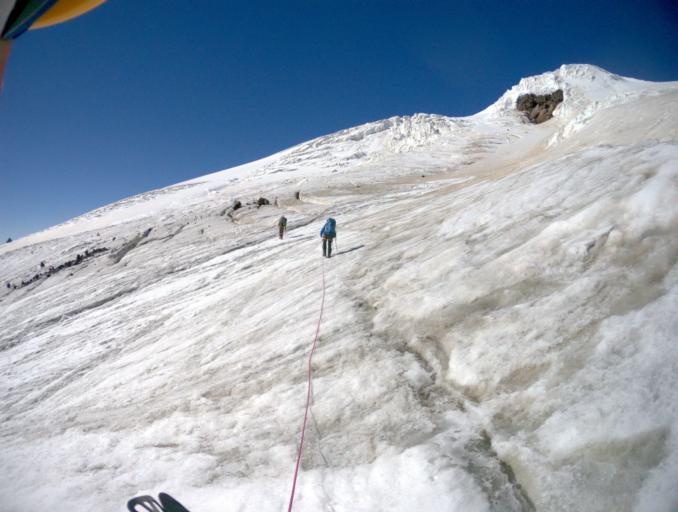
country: RU
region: Kabardino-Balkariya
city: Terskol
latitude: 43.3672
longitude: 42.4950
